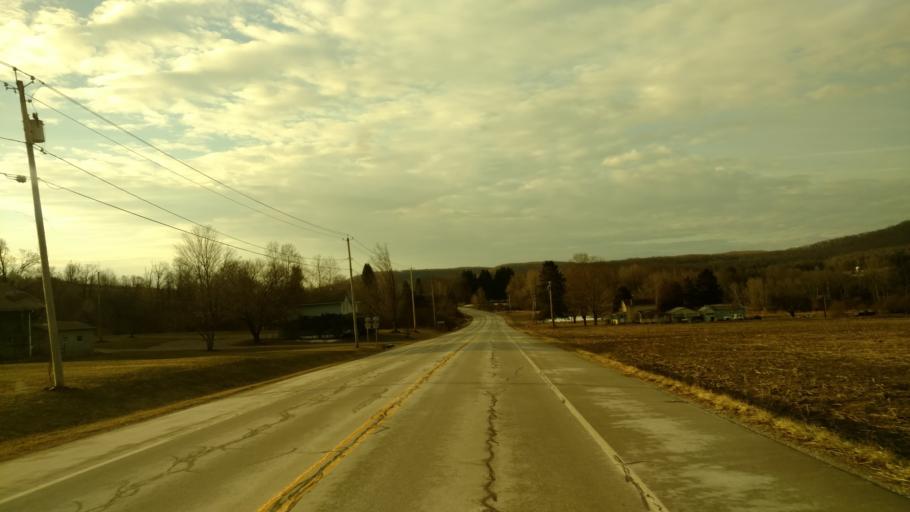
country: US
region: New York
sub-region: Allegany County
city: Wellsville
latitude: 42.0466
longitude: -77.9160
